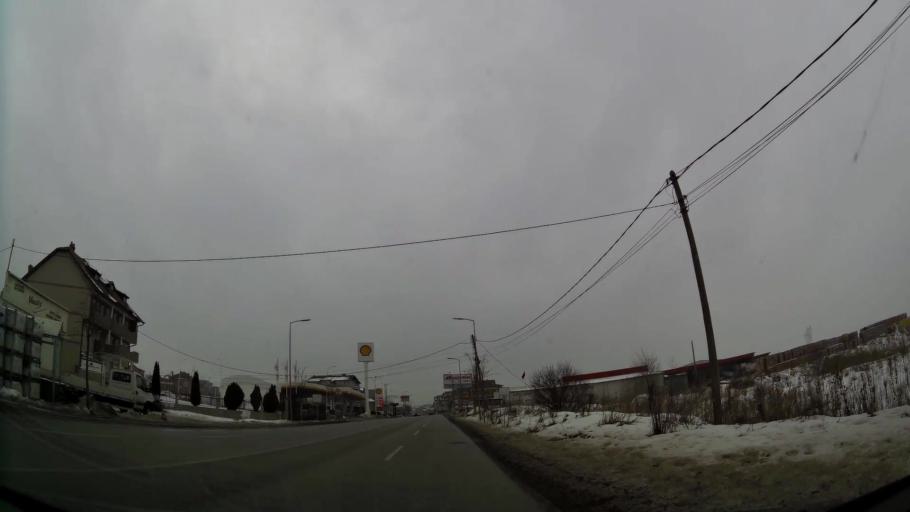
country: XK
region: Pristina
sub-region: Komuna e Prishtines
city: Pristina
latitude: 42.6987
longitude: 21.1594
